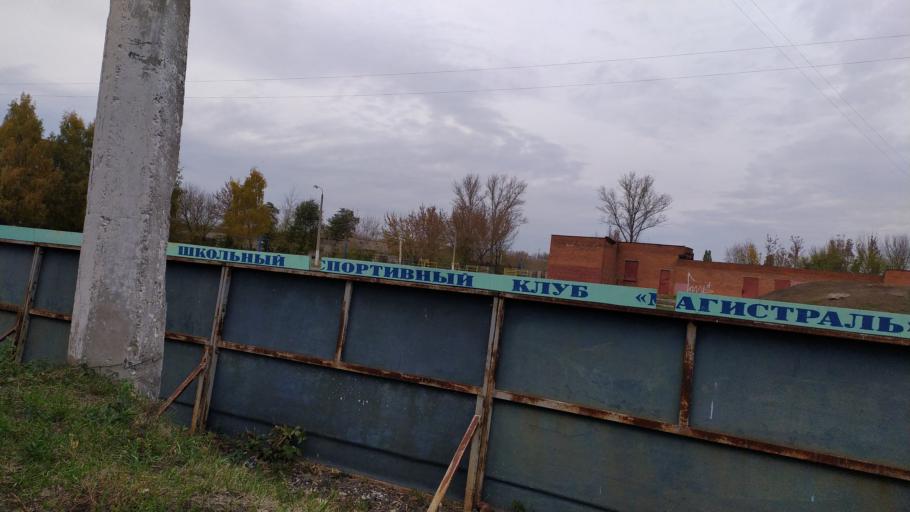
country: RU
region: Kursk
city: Kursk
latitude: 51.6503
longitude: 36.1446
